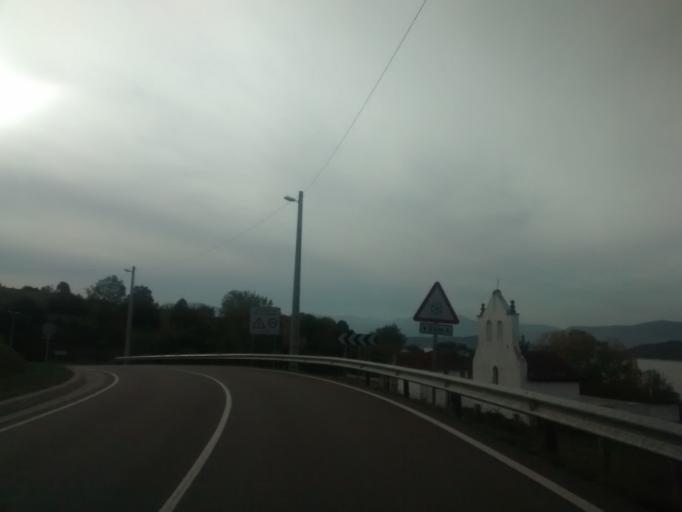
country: ES
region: Cantabria
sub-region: Provincia de Cantabria
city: San Miguel de Aguayo
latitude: 42.9726
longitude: -4.0258
